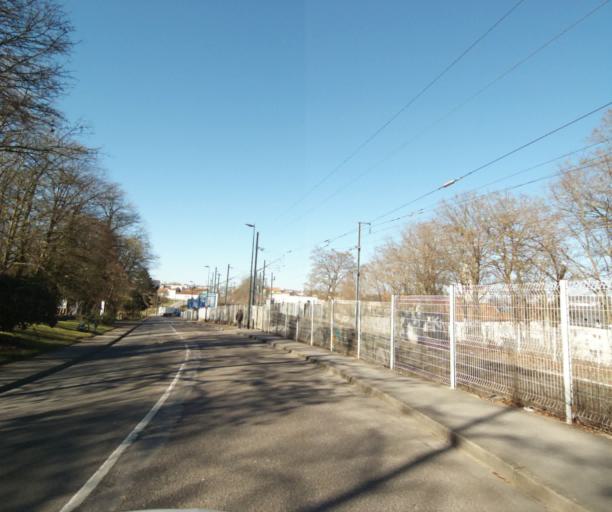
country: FR
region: Lorraine
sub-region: Departement de Meurthe-et-Moselle
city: Jarville-la-Malgrange
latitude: 48.6674
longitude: 6.2080
